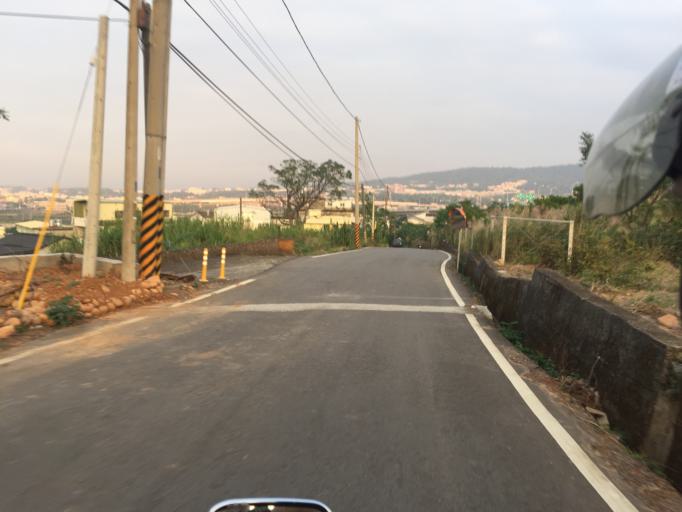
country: TW
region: Taiwan
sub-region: Miaoli
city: Miaoli
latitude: 24.4731
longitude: 120.7746
